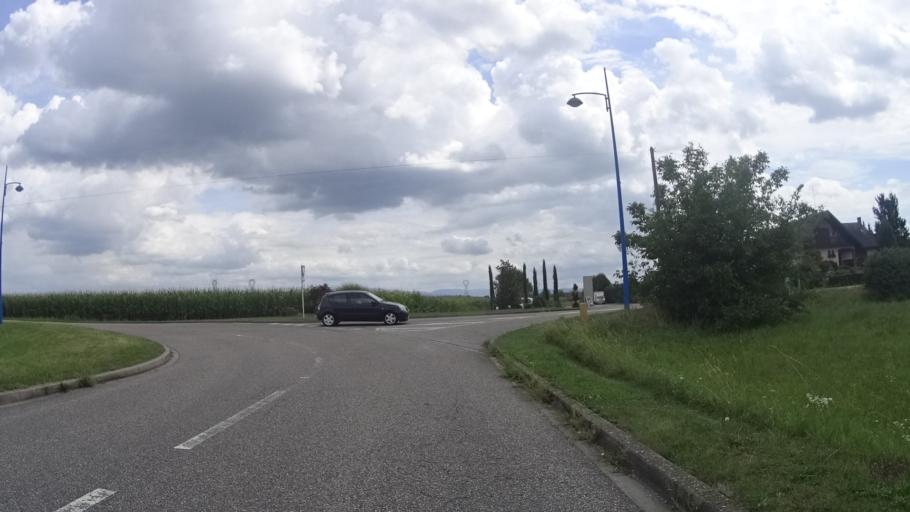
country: FR
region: Alsace
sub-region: Departement du Bas-Rhin
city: Gambsheim
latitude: 48.6983
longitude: 7.8922
